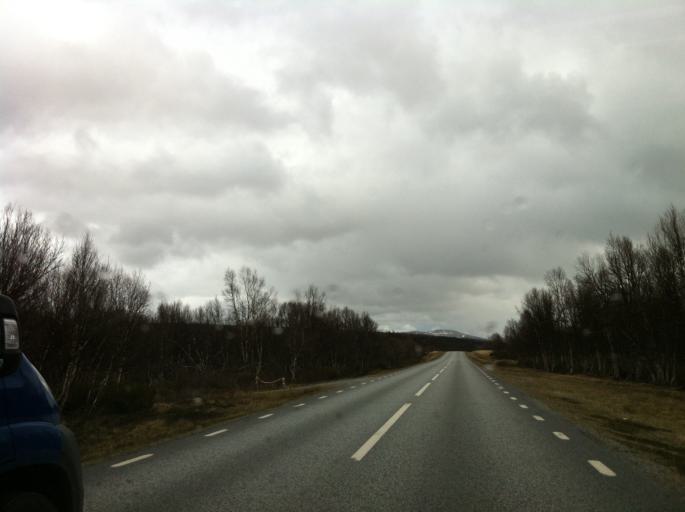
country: NO
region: Sor-Trondelag
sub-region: Tydal
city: Aas
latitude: 62.6382
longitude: 12.1023
